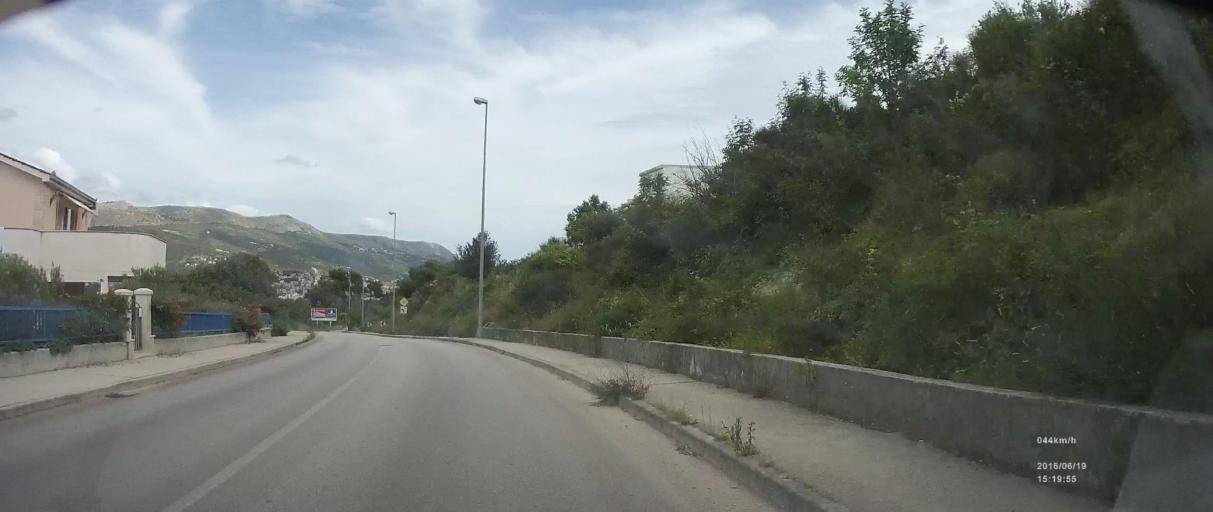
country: HR
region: Splitsko-Dalmatinska
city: Kamen
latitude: 43.5050
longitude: 16.5070
